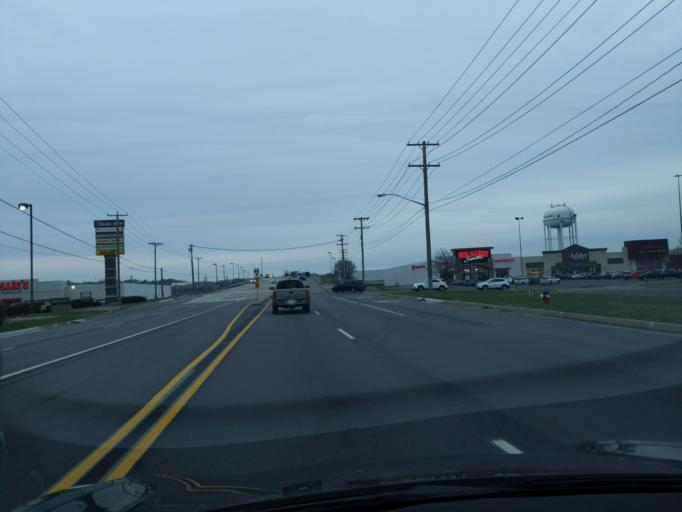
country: US
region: Indiana
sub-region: Saint Joseph County
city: Georgetown
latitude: 41.7131
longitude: -86.1876
